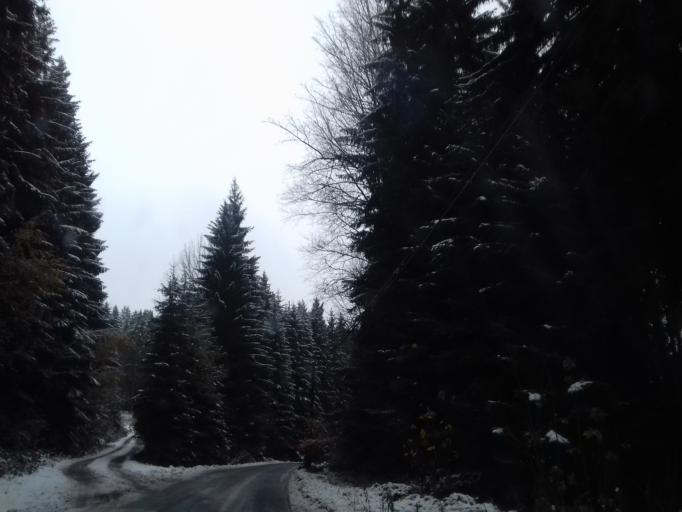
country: CZ
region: Plzensky
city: Postrekov
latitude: 49.4414
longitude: 12.7848
